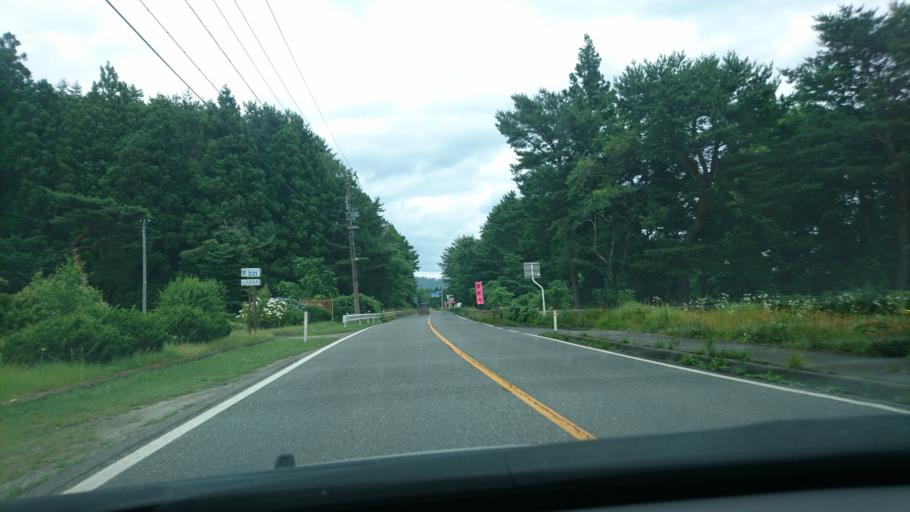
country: JP
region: Iwate
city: Yamada
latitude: 39.4068
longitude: 141.9575
